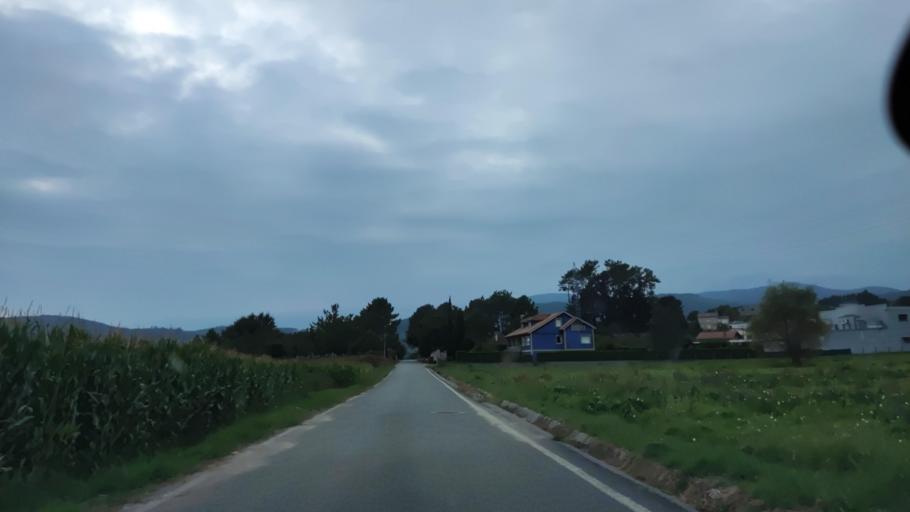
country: ES
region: Galicia
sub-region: Provincia da Coruna
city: Padron
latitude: 42.7137
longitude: -8.6987
